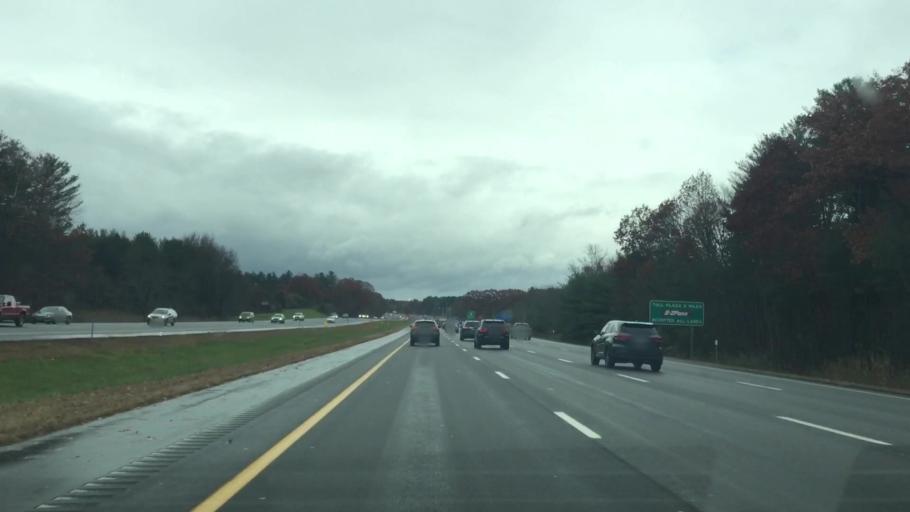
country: US
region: New Hampshire
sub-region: Rockingham County
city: Hampton Falls
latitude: 42.9262
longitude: -70.8666
